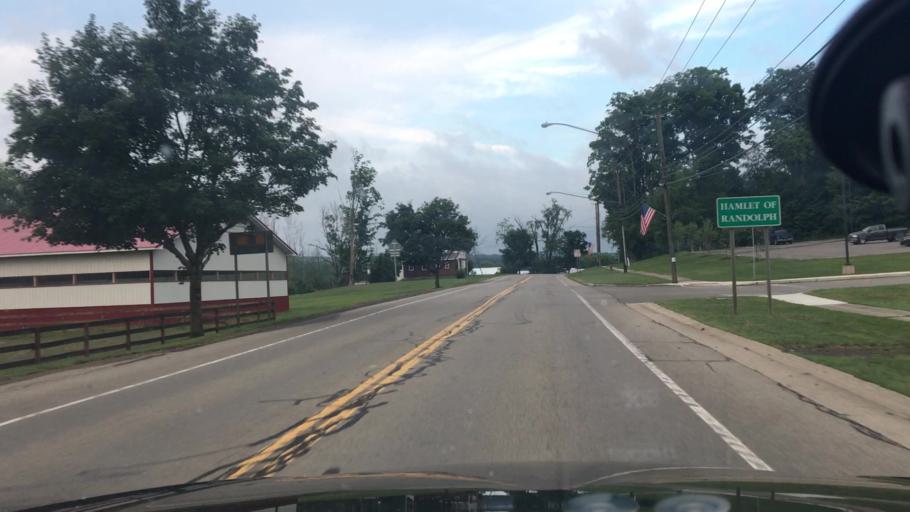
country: US
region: New York
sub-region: Cattaraugus County
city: Randolph
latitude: 42.1657
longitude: -78.9636
